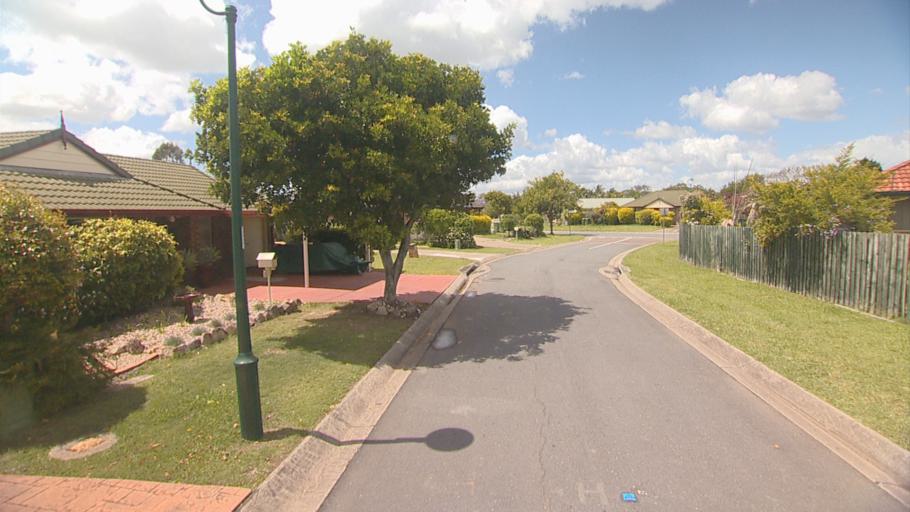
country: AU
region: Queensland
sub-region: Logan
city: Beenleigh
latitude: -27.6951
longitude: 153.1836
